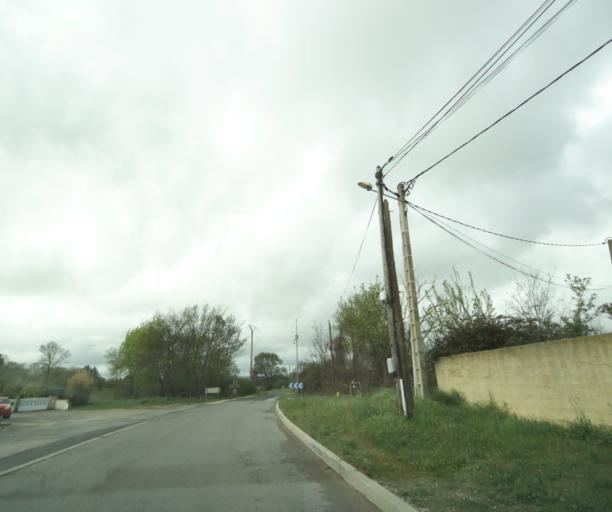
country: FR
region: Languedoc-Roussillon
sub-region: Departement de l'Herault
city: Fabregues
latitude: 43.5544
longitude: 3.7647
